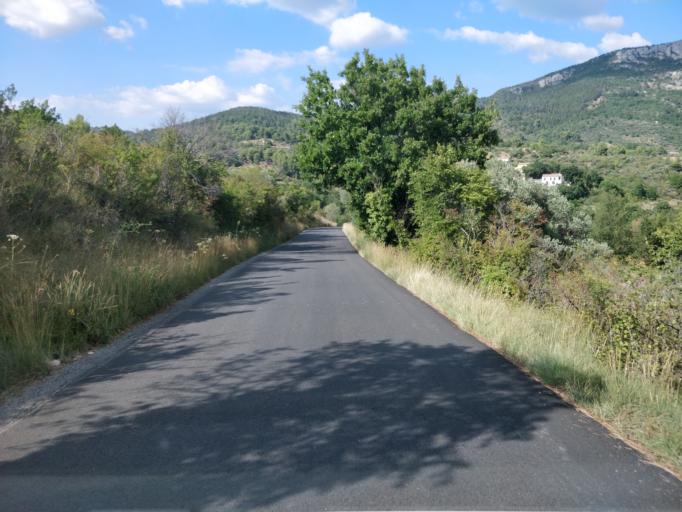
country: FR
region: Provence-Alpes-Cote d'Azur
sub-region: Departement des Alpes-de-Haute-Provence
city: Riez
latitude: 43.8399
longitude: 6.2077
